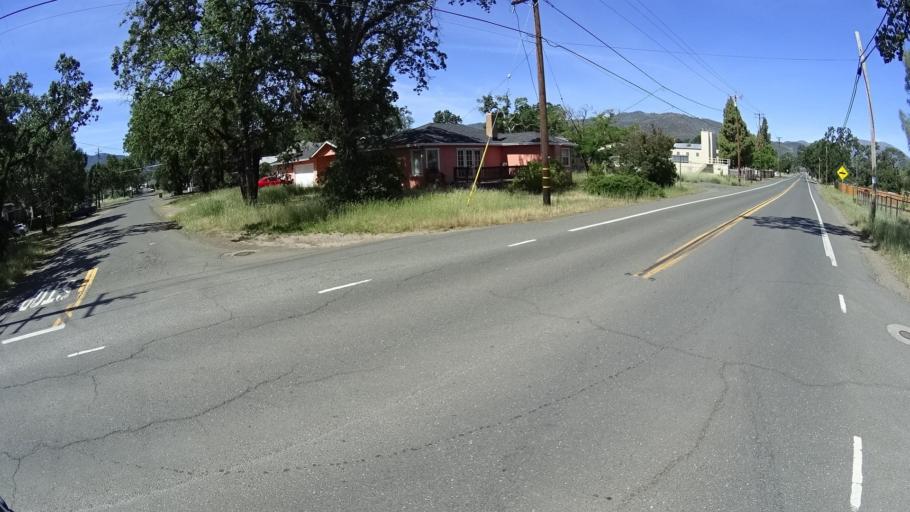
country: US
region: California
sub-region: Lake County
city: Middletown
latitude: 38.7535
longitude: -122.6200
